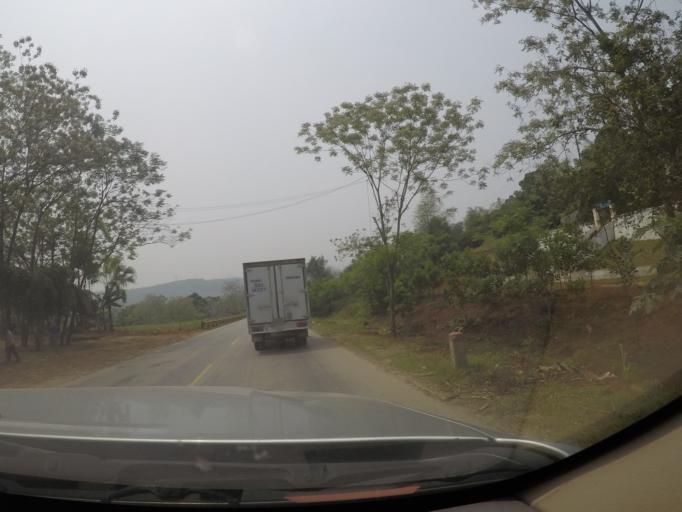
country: VN
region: Thanh Hoa
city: Thi Tran Thuong Xuan
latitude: 19.9709
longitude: 105.4018
